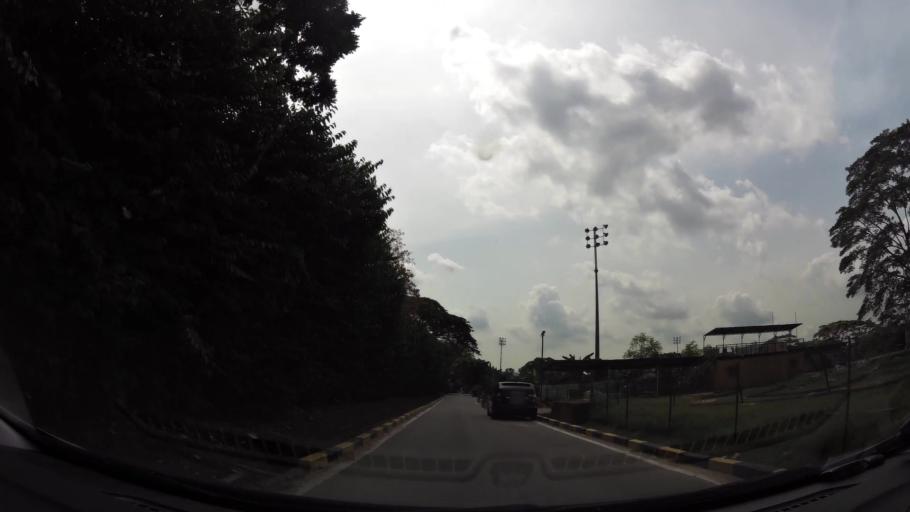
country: SG
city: Singapore
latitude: 1.3405
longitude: 103.7962
